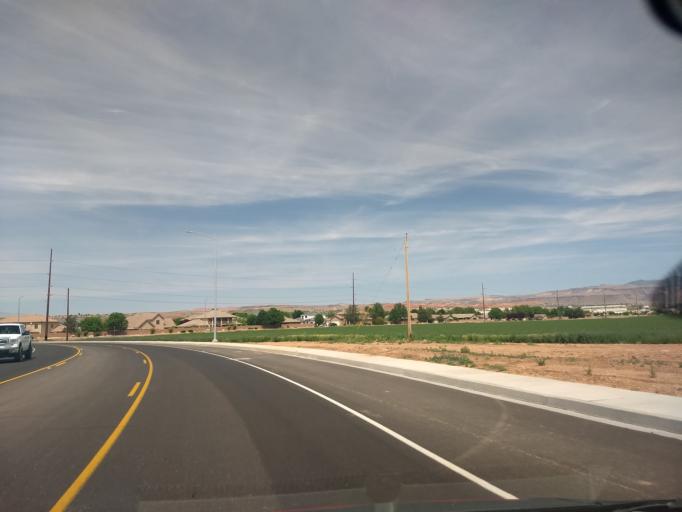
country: US
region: Utah
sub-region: Washington County
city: Washington
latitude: 37.0958
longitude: -113.5073
